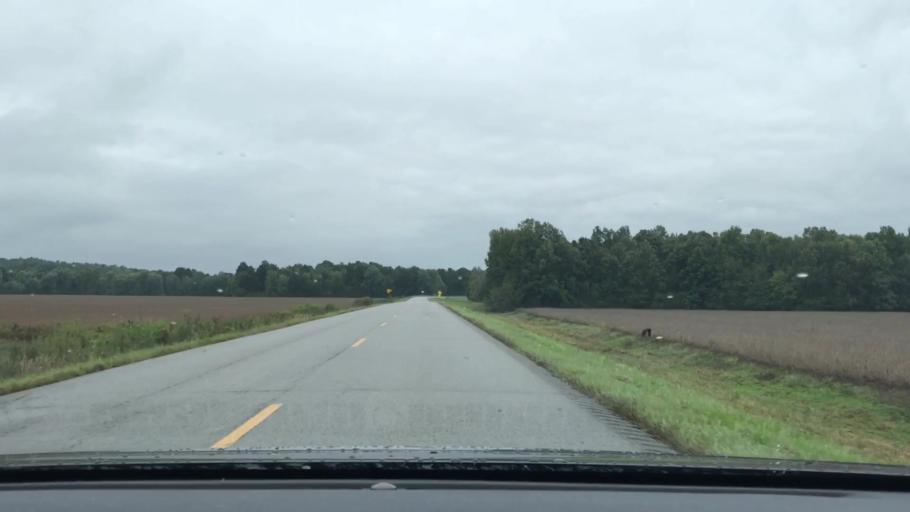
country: US
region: Kentucky
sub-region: McLean County
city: Calhoun
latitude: 37.4948
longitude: -87.2463
